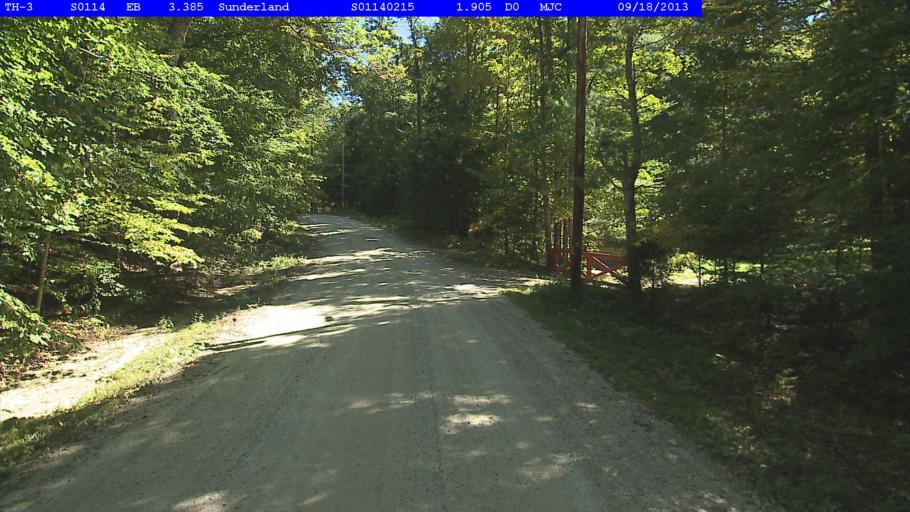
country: US
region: Vermont
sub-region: Bennington County
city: Arlington
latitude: 43.0462
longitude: -73.1161
